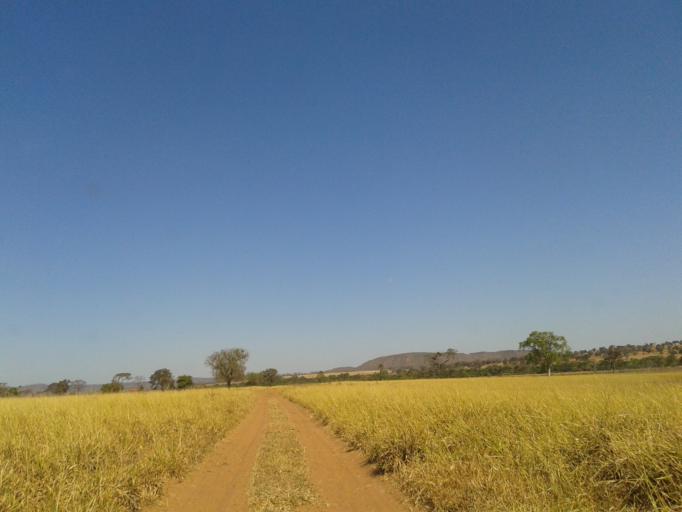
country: BR
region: Minas Gerais
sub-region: Santa Vitoria
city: Santa Vitoria
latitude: -19.1539
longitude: -50.0281
